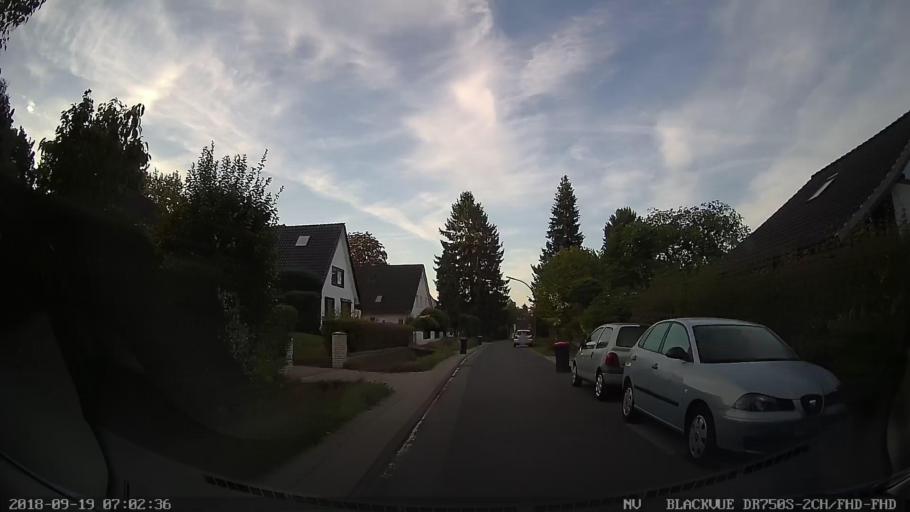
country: DE
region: Hamburg
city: Eidelstedt
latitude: 53.6266
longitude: 9.9010
